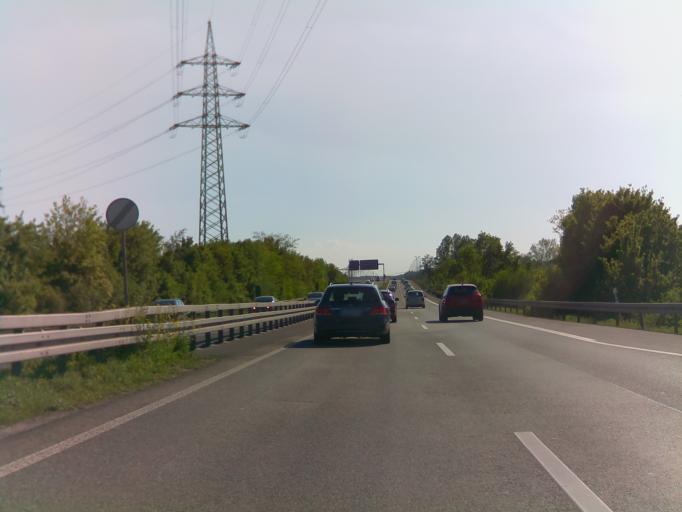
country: DE
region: Hesse
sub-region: Regierungsbezirk Darmstadt
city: Hanau am Main
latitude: 50.1123
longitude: 8.9297
